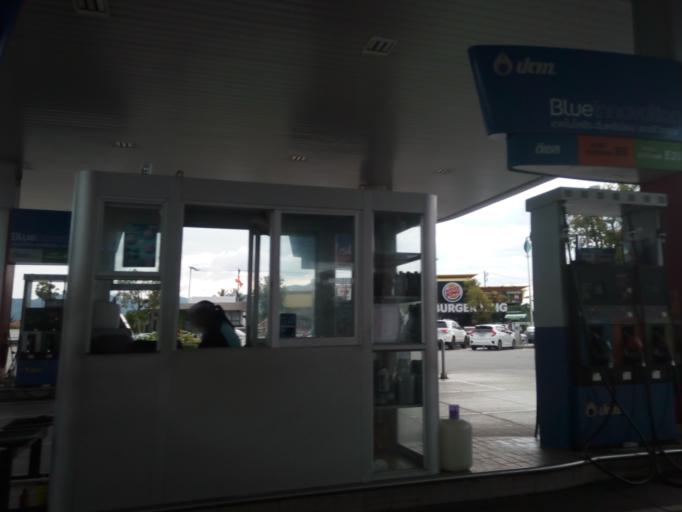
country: TH
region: Phuket
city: Thalang
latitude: 8.0050
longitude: 98.3436
